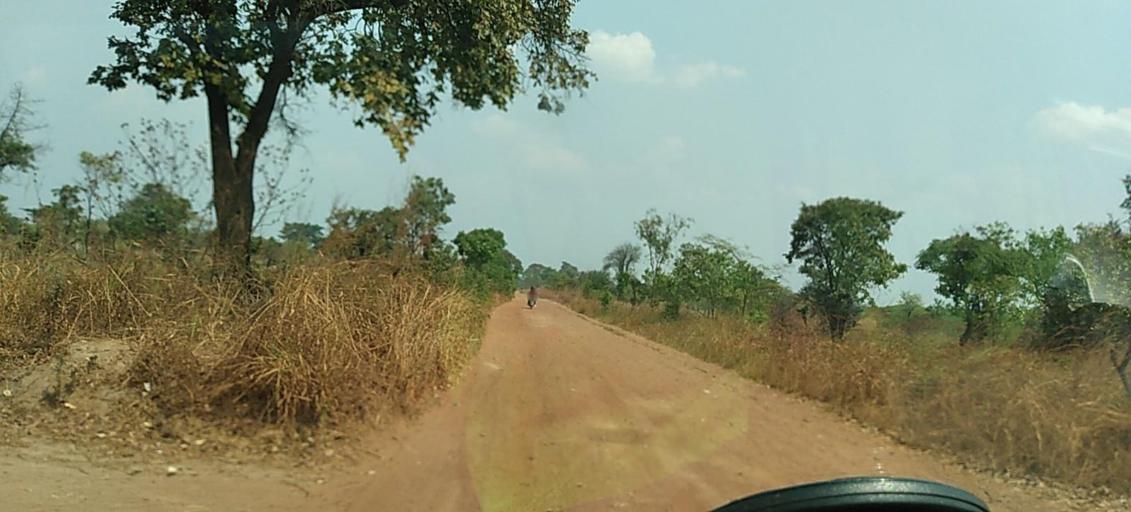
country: ZM
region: North-Western
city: Kansanshi
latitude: -12.1005
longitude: 26.3639
